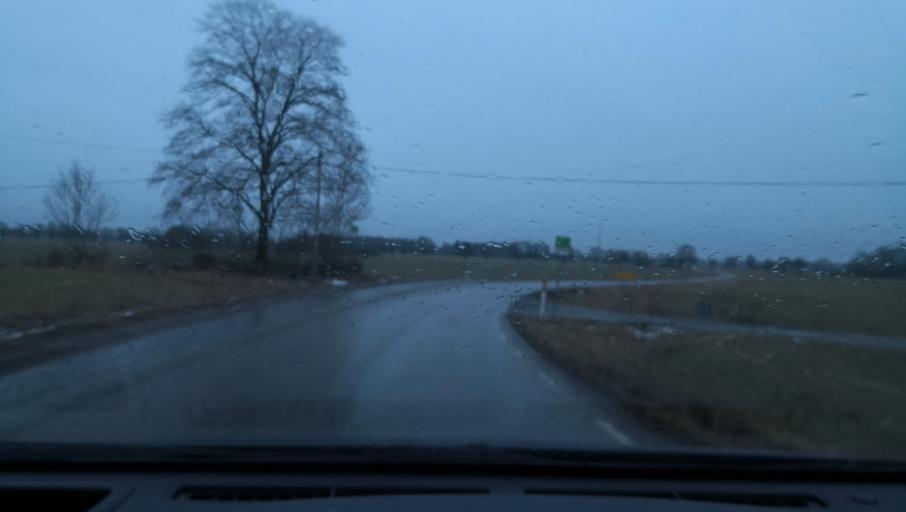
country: SE
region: Soedermanland
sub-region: Eskilstuna Kommun
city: Arla
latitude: 59.4479
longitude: 16.7235
